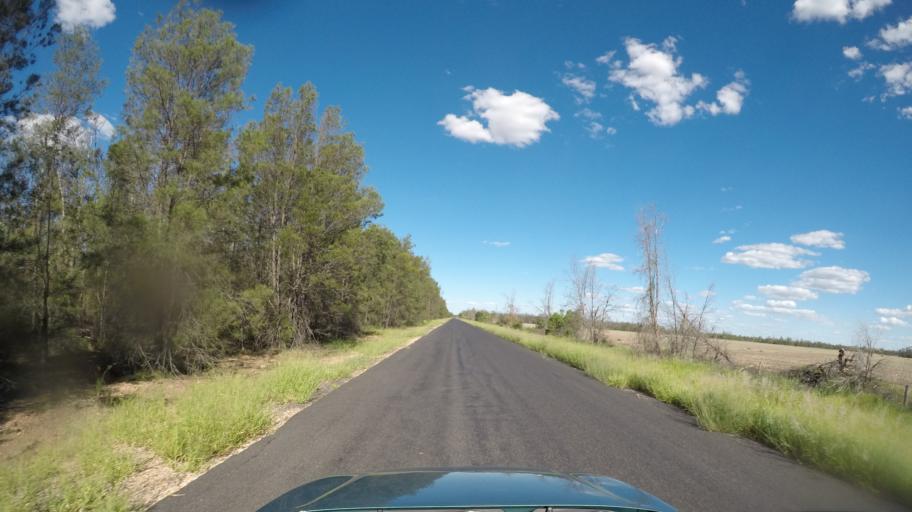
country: AU
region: Queensland
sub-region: Goondiwindi
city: Goondiwindi
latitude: -28.1657
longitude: 150.4394
